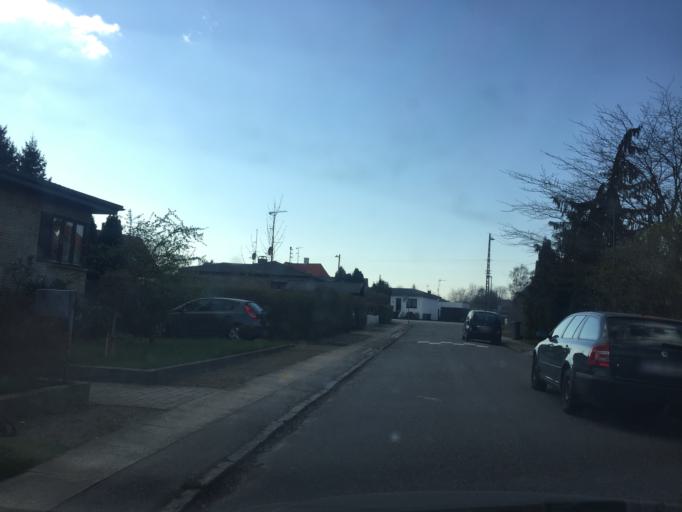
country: DK
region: Capital Region
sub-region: Herlev Kommune
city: Herlev
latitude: 55.7073
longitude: 12.4600
